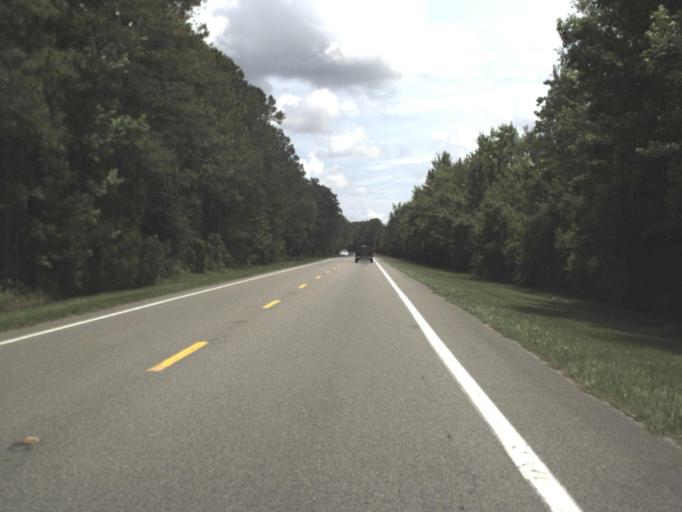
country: US
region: Florida
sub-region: Nassau County
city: Yulee
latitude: 30.6567
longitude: -81.6295
